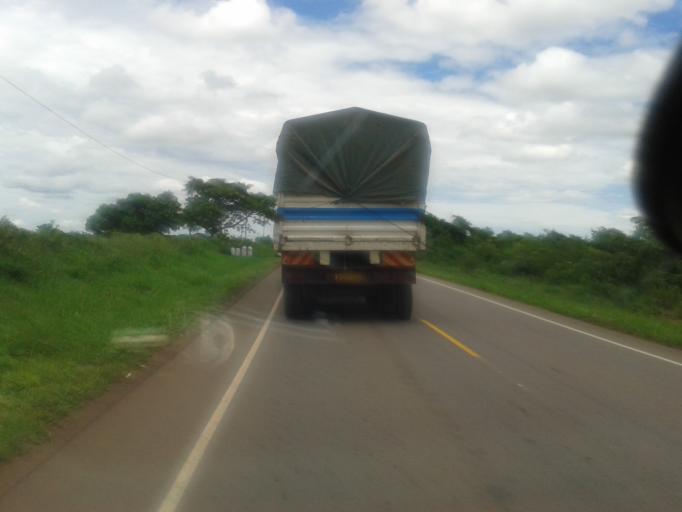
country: UG
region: Western Region
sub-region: Kiryandongo District
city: Masindi Port
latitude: 1.7444
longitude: 32.0231
